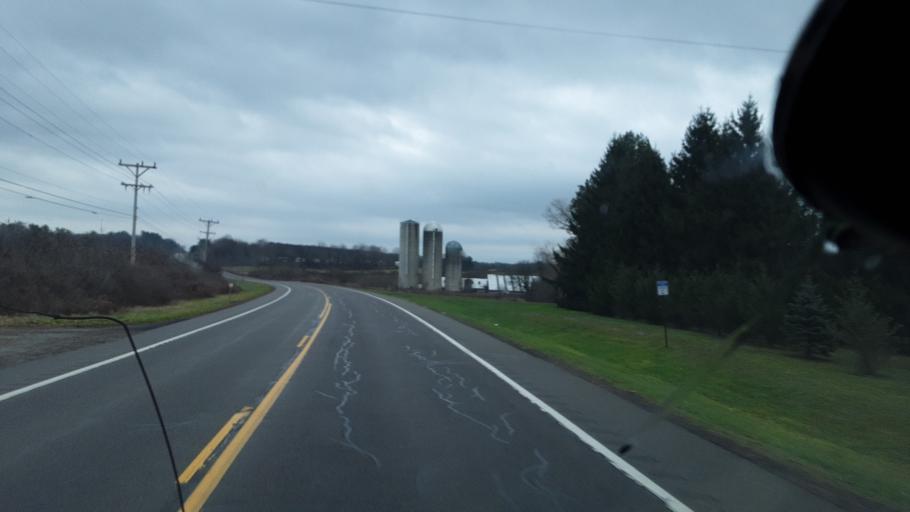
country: US
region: New York
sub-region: Allegany County
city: Houghton
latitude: 42.3890
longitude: -78.2087
